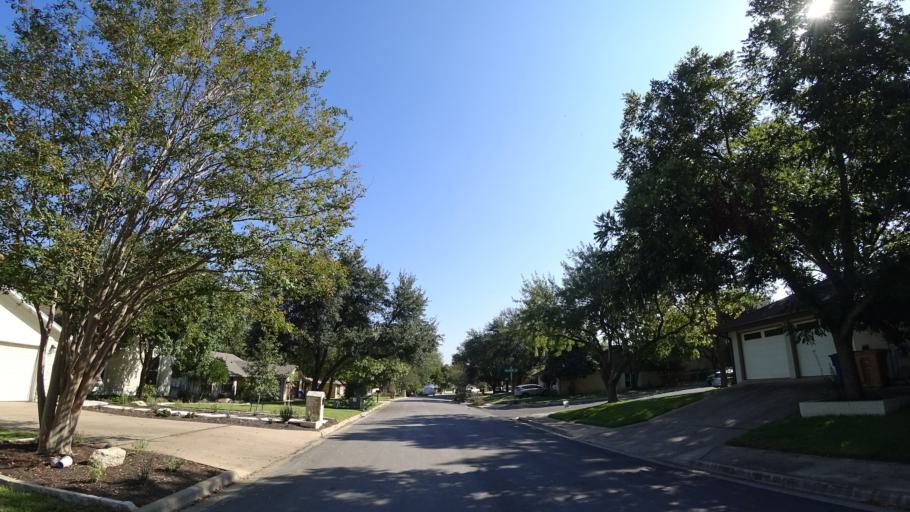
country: US
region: Texas
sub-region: Travis County
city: Rollingwood
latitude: 30.2680
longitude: -97.8100
